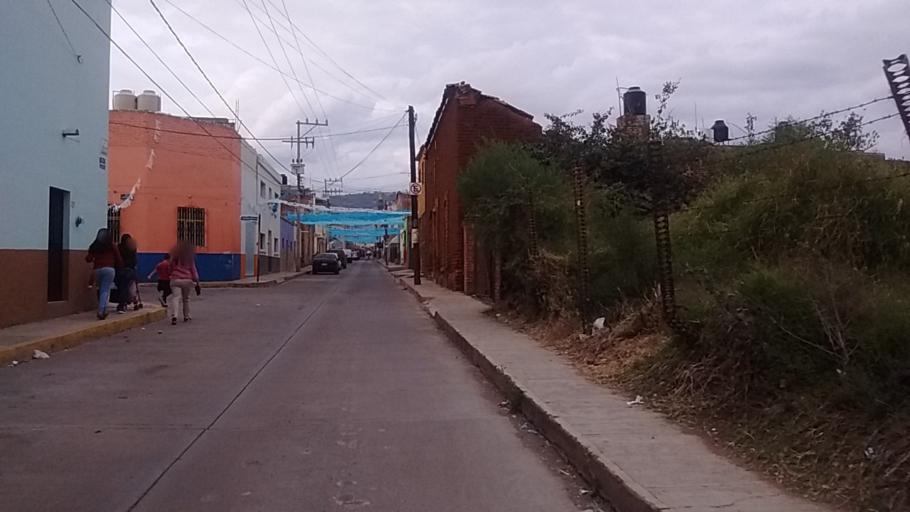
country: MX
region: Jalisco
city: Atotonilco el Alto
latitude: 20.5452
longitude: -102.5073
